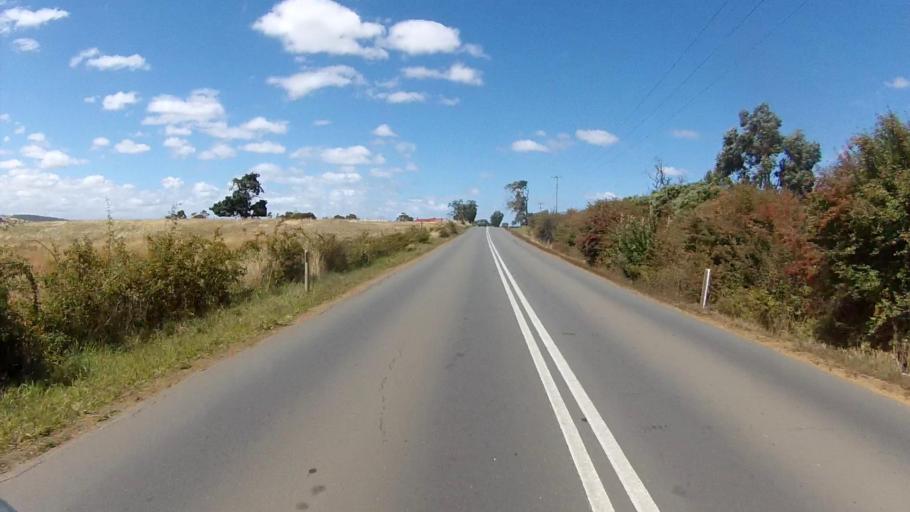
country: AU
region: Tasmania
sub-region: Clarence
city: Cambridge
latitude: -42.7736
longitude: 147.4154
